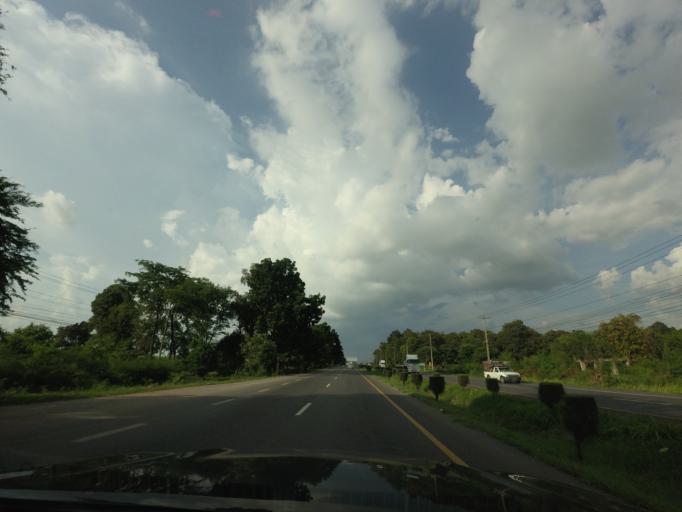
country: TH
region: Khon Kaen
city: Ban Haet
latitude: 16.2754
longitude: 102.7829
